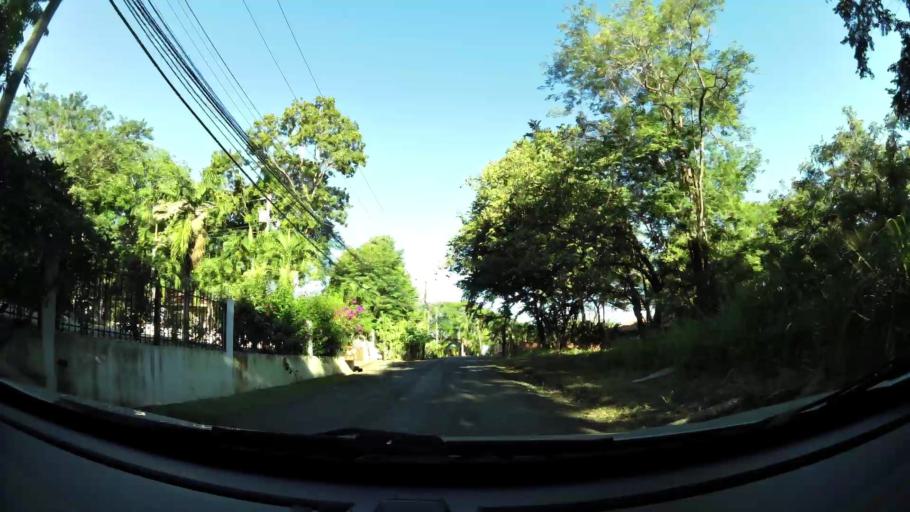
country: CR
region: Guanacaste
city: Sardinal
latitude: 10.5682
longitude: -85.6764
